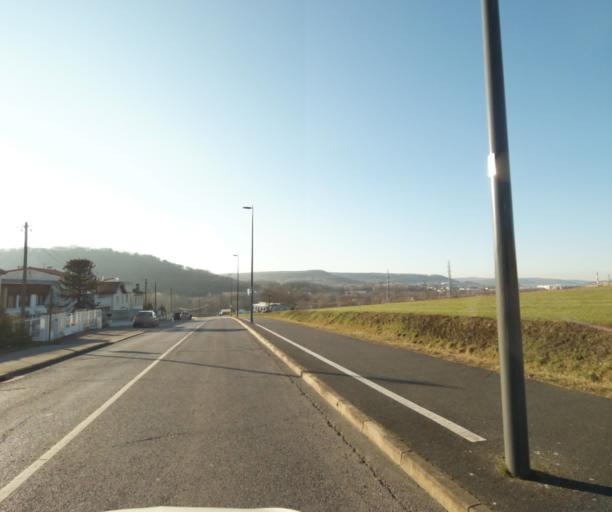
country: FR
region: Lorraine
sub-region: Departement de Meurthe-et-Moselle
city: Malzeville
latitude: 48.7250
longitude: 6.1804
